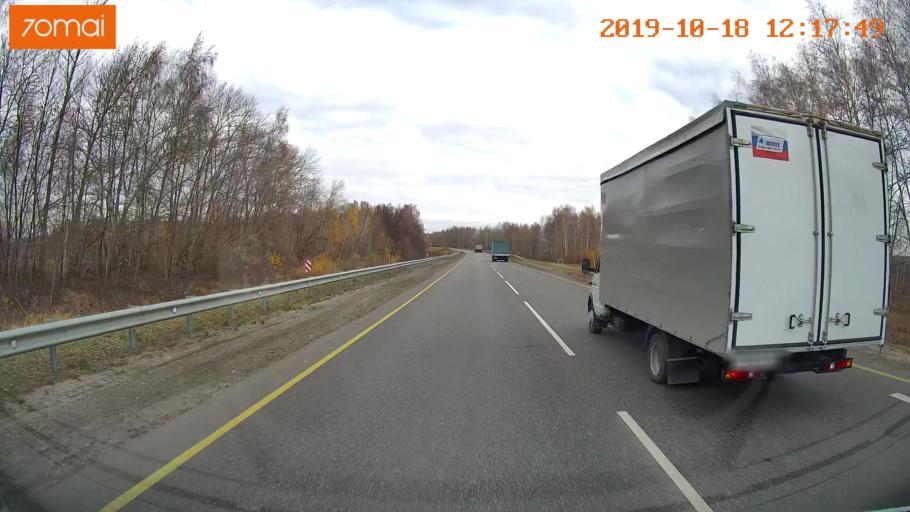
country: RU
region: Rjazan
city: Zakharovo
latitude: 54.4605
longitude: 39.4495
